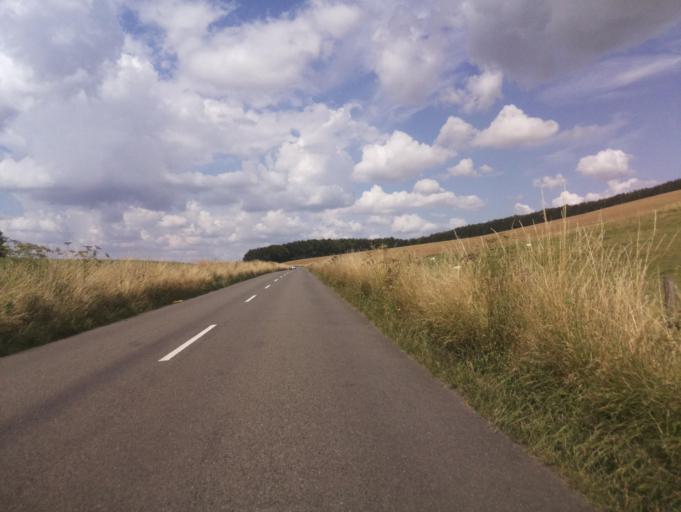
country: GB
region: England
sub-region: Borough of Swindon
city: Bishopstone
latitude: 51.5466
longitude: -1.5949
